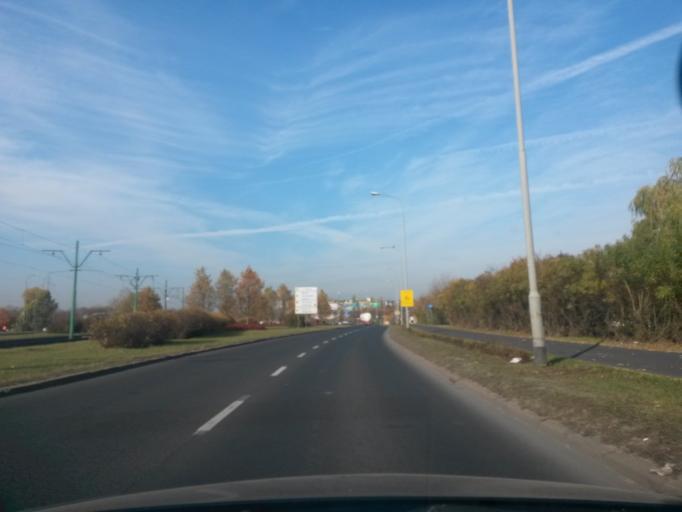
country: PL
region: Greater Poland Voivodeship
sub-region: Poznan
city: Poznan
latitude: 52.3791
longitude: 16.9472
